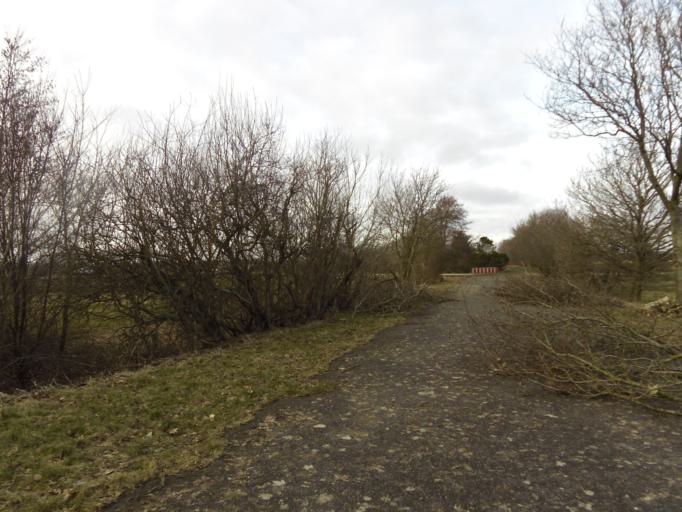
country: DK
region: South Denmark
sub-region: Tonder Kommune
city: Toftlund
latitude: 55.2349
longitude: 9.1254
